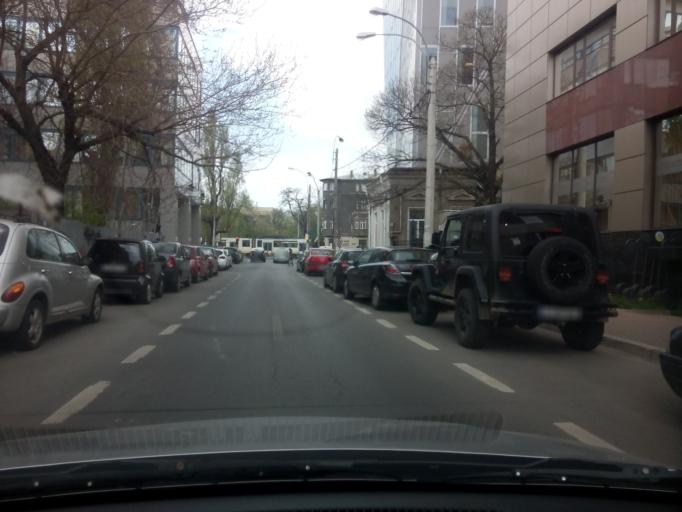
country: RO
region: Bucuresti
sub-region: Municipiul Bucuresti
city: Bucharest
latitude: 44.4520
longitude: 26.0953
